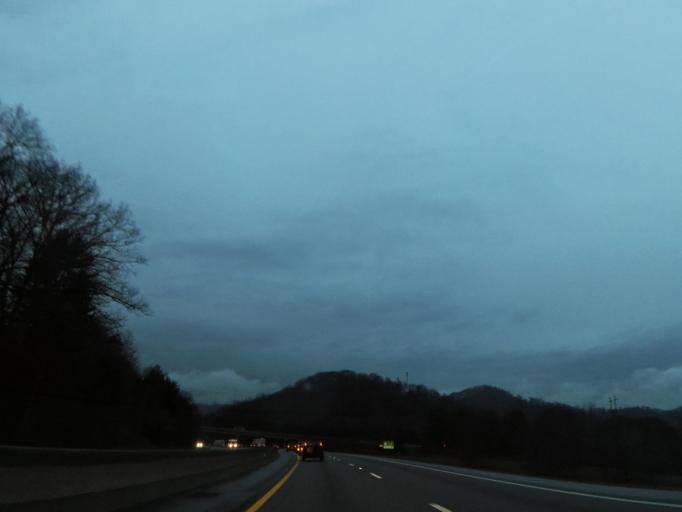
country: US
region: North Carolina
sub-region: Haywood County
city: Canton
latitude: 35.5500
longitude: -82.8159
